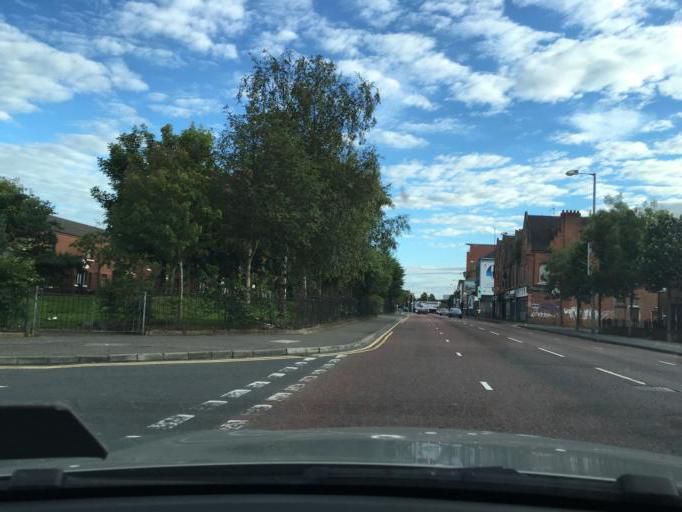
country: GB
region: Northern Ireland
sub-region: City of Belfast
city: Belfast
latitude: 54.5941
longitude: -5.9245
